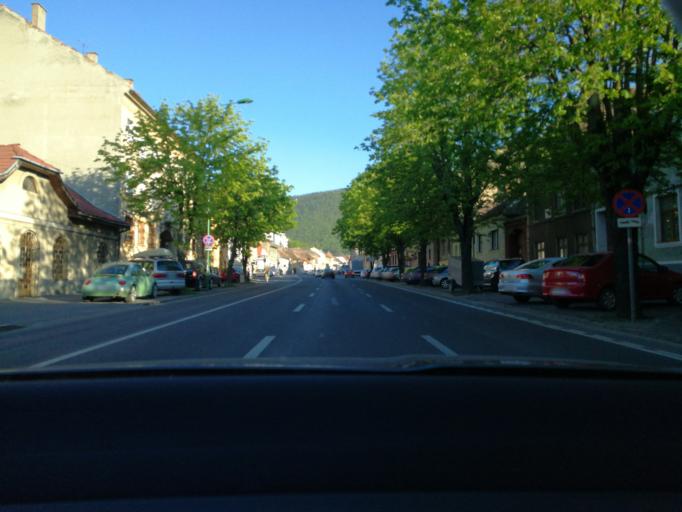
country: RO
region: Brasov
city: Brasov
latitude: 45.6530
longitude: 25.5846
